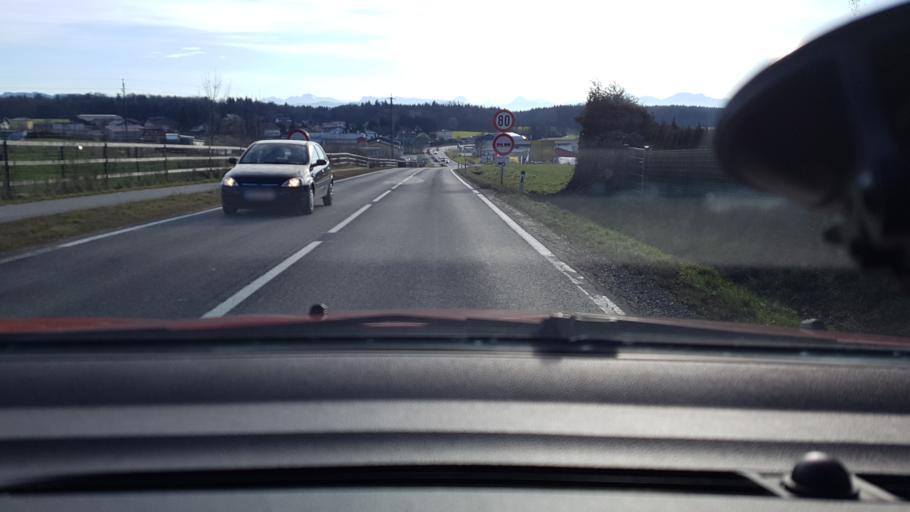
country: AT
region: Salzburg
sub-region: Politischer Bezirk Salzburg-Umgebung
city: Dorfbeuern
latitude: 48.0419
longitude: 12.9885
